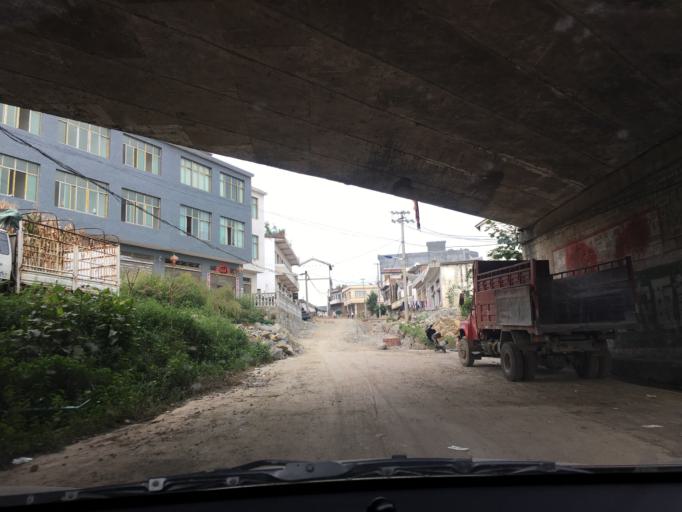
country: CN
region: Guangxi Zhuangzu Zizhiqu
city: Xinzhou
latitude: 25.4598
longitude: 105.4889
